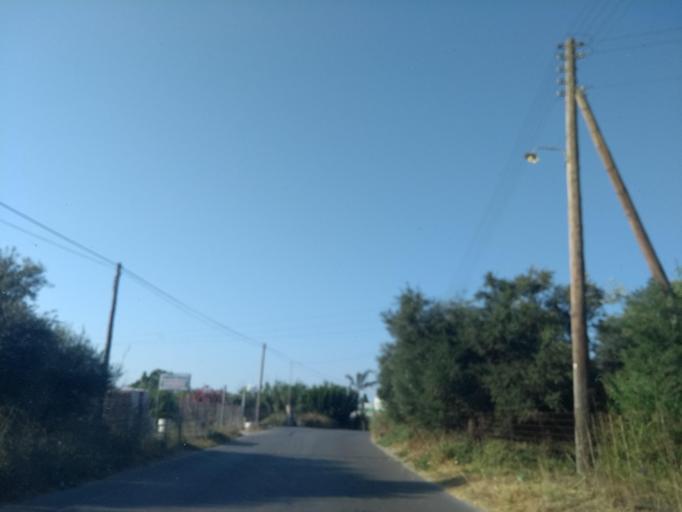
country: GR
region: Crete
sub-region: Nomos Chanias
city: Kalivai
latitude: 35.4458
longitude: 24.1709
